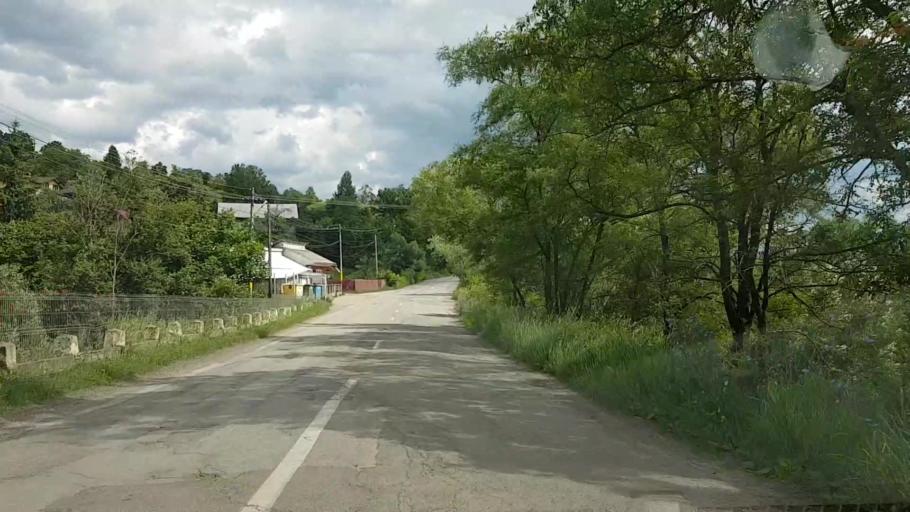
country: RO
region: Neamt
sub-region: Comuna Hangu
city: Hangu
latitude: 47.0426
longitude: 26.0552
